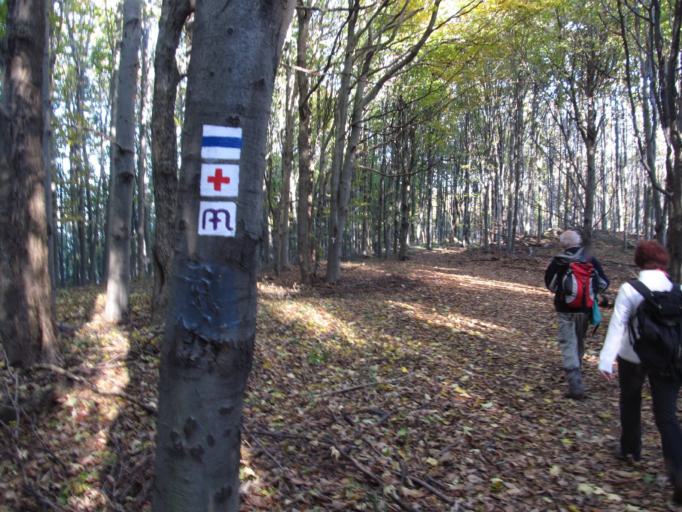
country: HU
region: Heves
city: Paradsasvar
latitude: 47.9171
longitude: 19.9341
